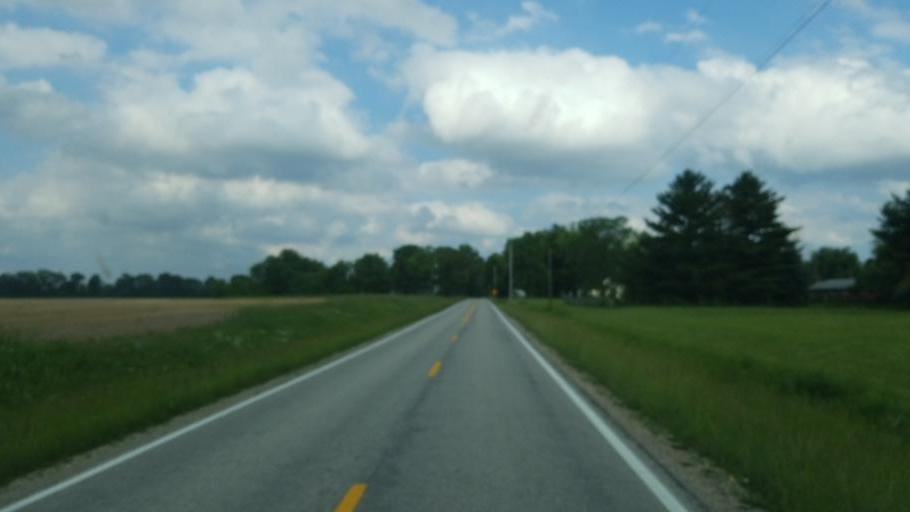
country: US
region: Ohio
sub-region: Delaware County
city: Sunbury
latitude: 40.2160
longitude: -82.8365
